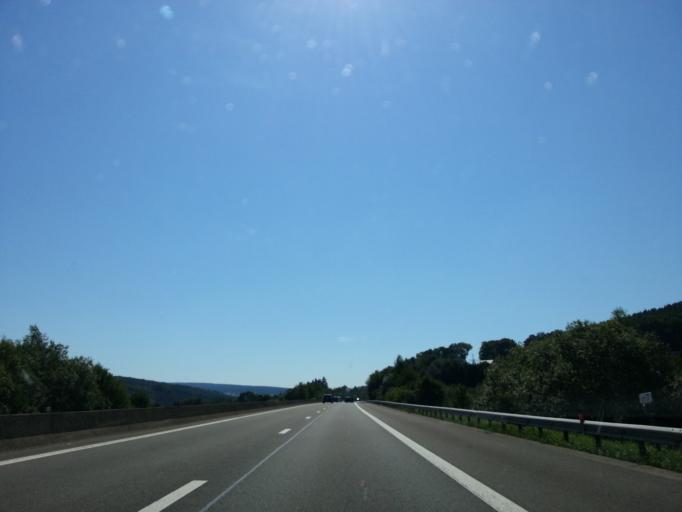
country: BE
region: Wallonia
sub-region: Province de Liege
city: Malmedy
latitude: 50.3818
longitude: 6.0009
